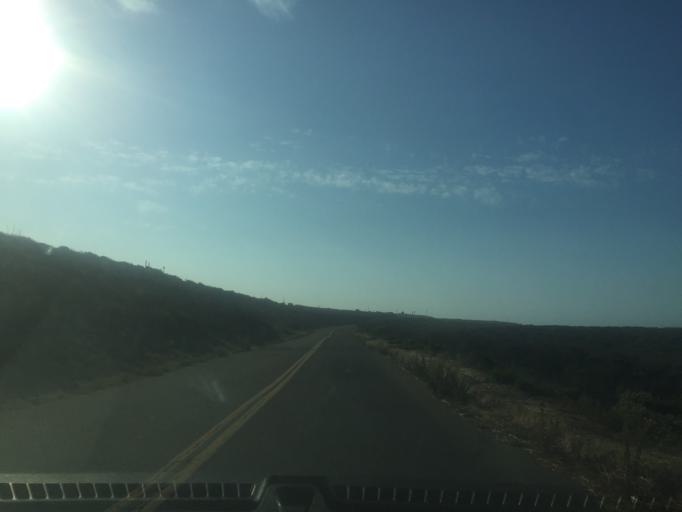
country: US
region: California
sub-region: Santa Barbara County
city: Lompoc
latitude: 34.5041
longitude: -120.4983
